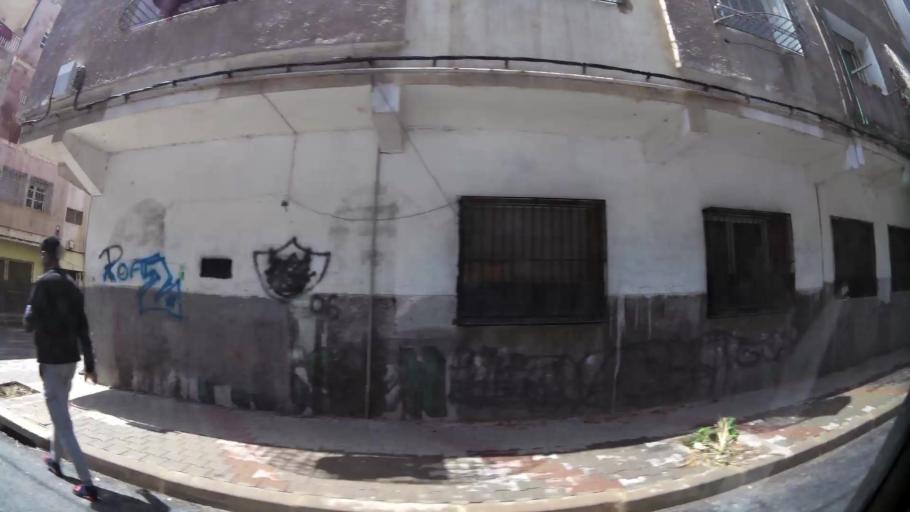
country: MA
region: Grand Casablanca
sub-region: Mediouna
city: Tit Mellil
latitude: 33.5416
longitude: -7.5518
